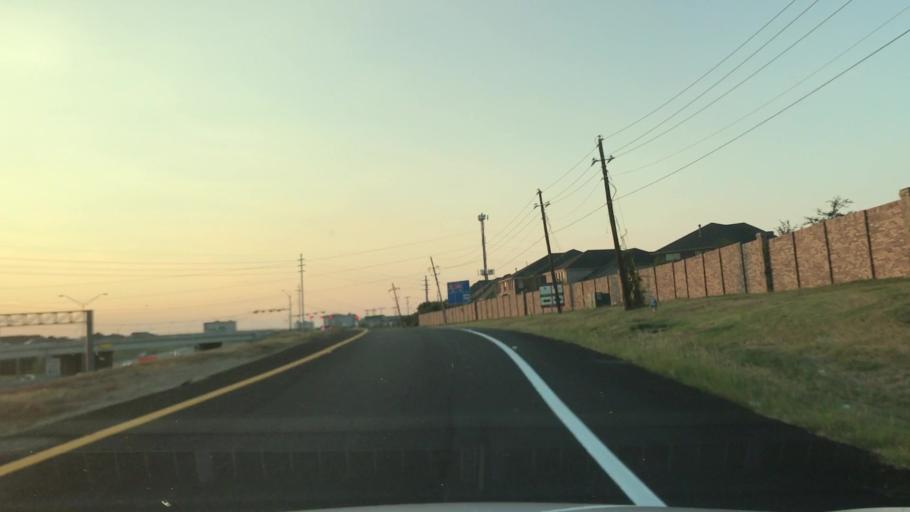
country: US
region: Texas
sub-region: Dallas County
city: Coppell
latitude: 32.9048
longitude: -96.9905
